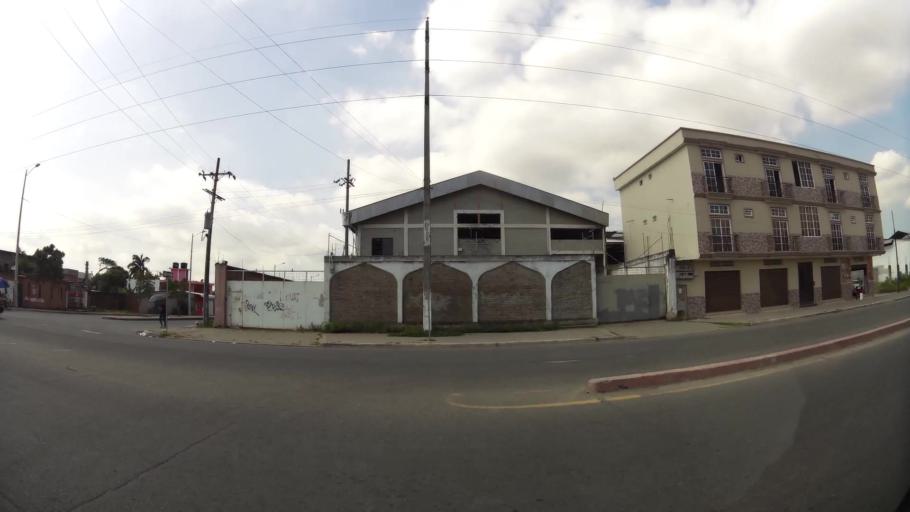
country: EC
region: Guayas
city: Eloy Alfaro
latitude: -2.1660
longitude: -79.8371
